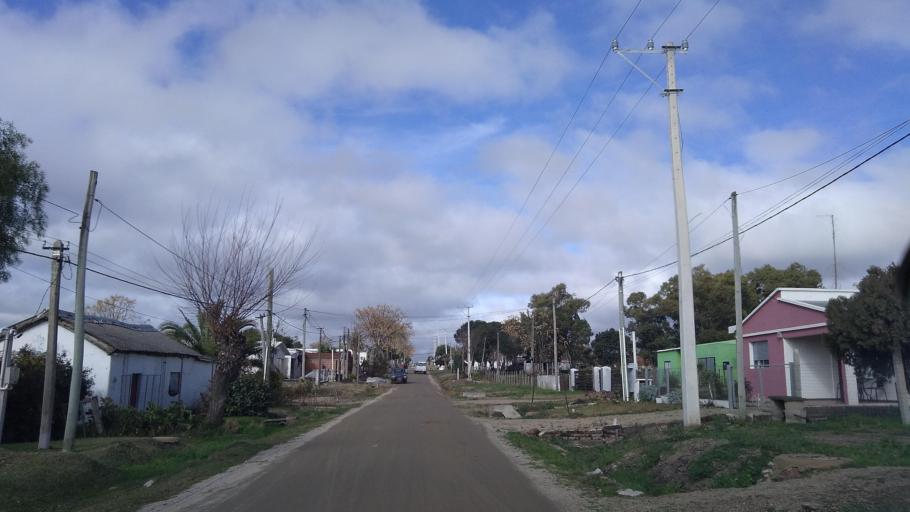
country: UY
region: Canelones
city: Tala
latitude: -34.1920
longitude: -55.7418
